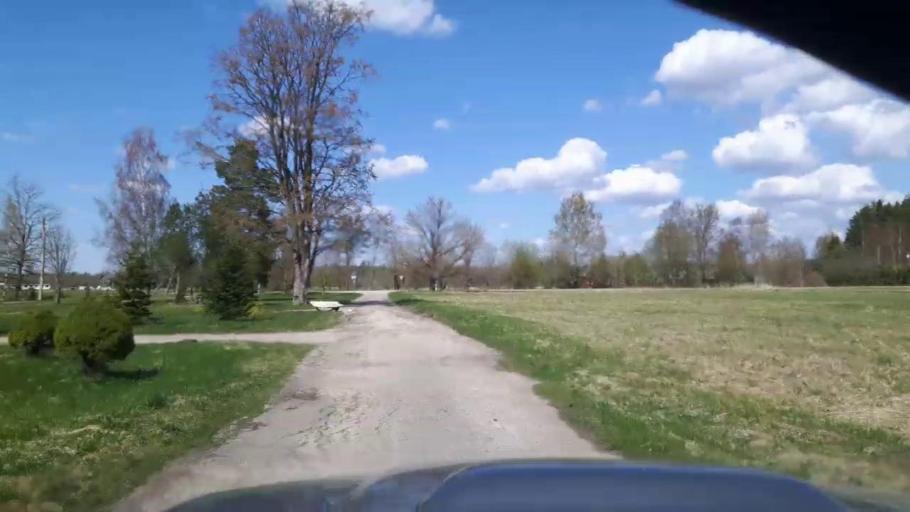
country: EE
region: Paernumaa
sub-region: Tootsi vald
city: Tootsi
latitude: 58.4993
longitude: 24.9241
